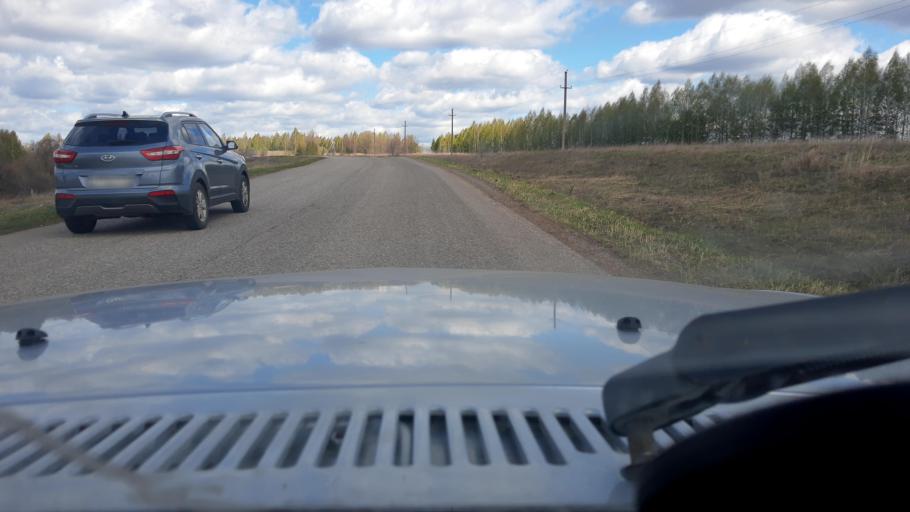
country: RU
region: Bashkortostan
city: Pavlovka
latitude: 55.3659
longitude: 56.4209
